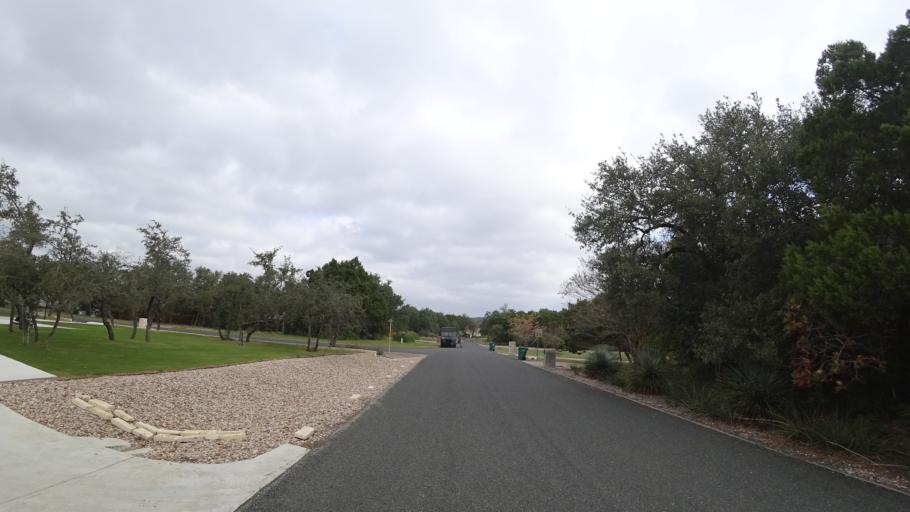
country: US
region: Texas
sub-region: Travis County
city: Barton Creek
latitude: 30.2523
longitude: -97.9096
